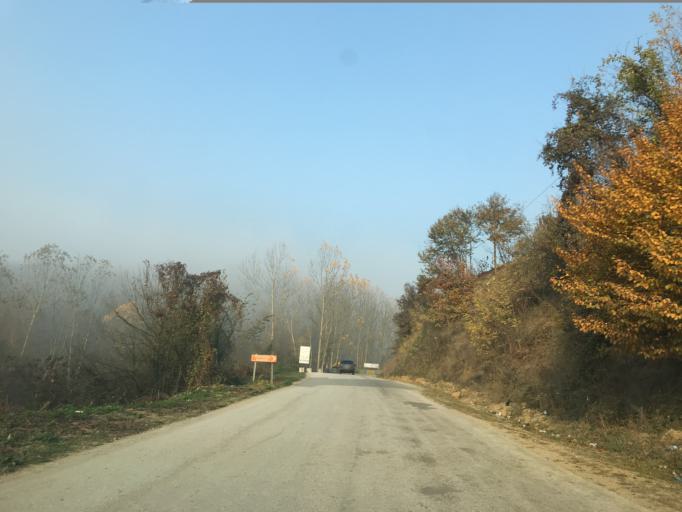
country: TR
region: Duzce
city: Cumayeri
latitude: 40.9038
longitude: 30.9530
